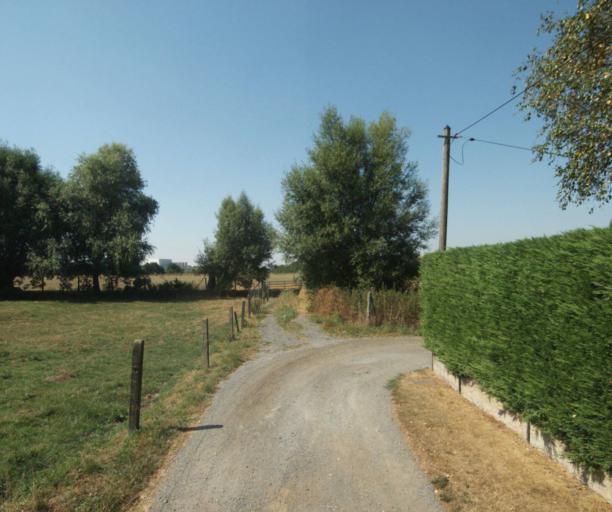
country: FR
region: Nord-Pas-de-Calais
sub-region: Departement du Nord
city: Bousbecque
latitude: 50.7689
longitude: 3.0935
